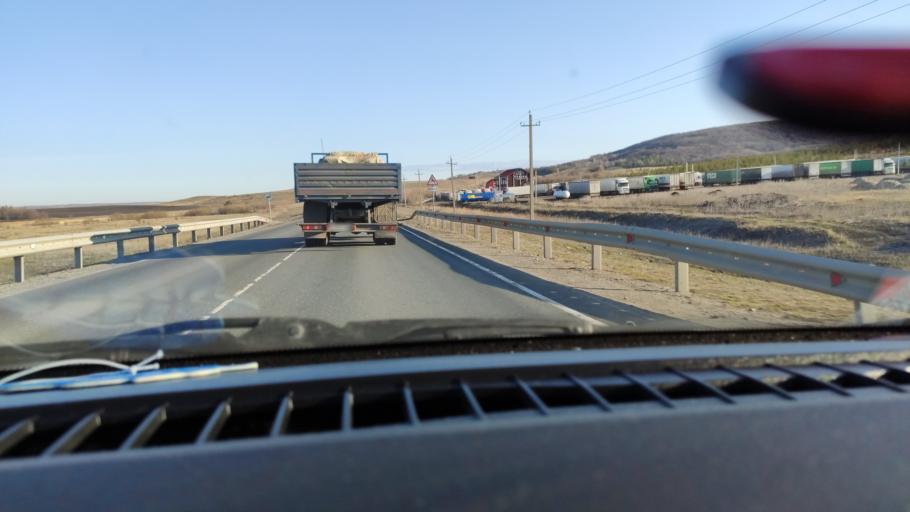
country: RU
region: Saratov
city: Alekseyevka
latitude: 52.3073
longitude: 47.9256
